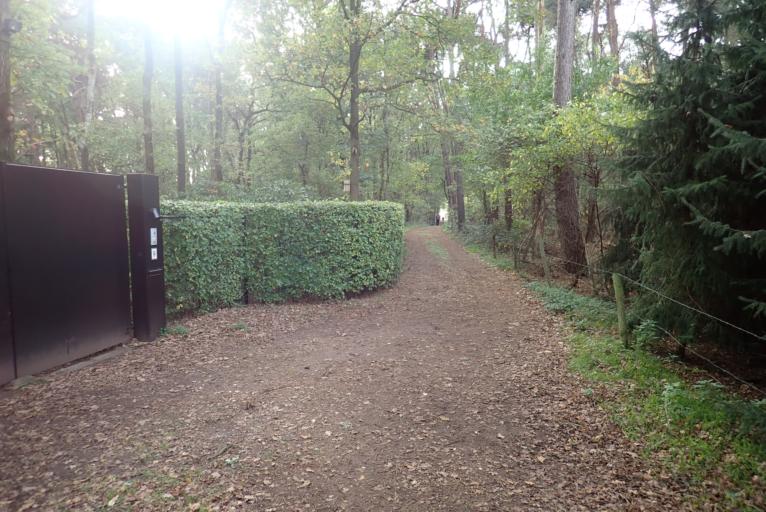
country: BE
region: Flanders
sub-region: Provincie Antwerpen
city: Wuustwezel
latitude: 51.3931
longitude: 4.5737
